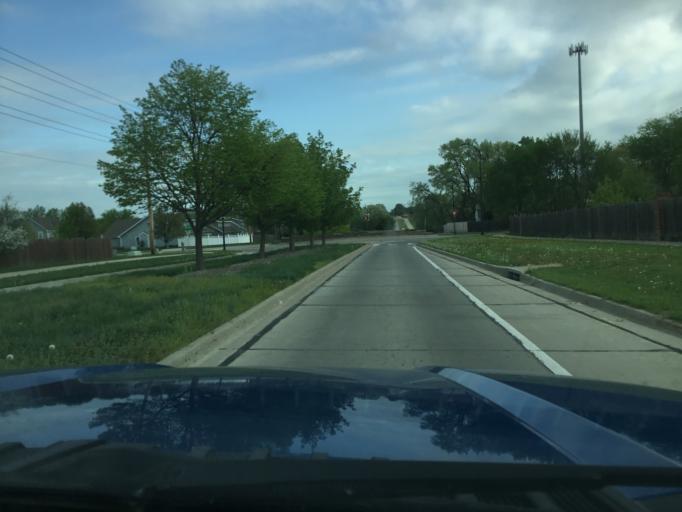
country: US
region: Kansas
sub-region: Douglas County
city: Lawrence
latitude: 38.9925
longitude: -95.2790
